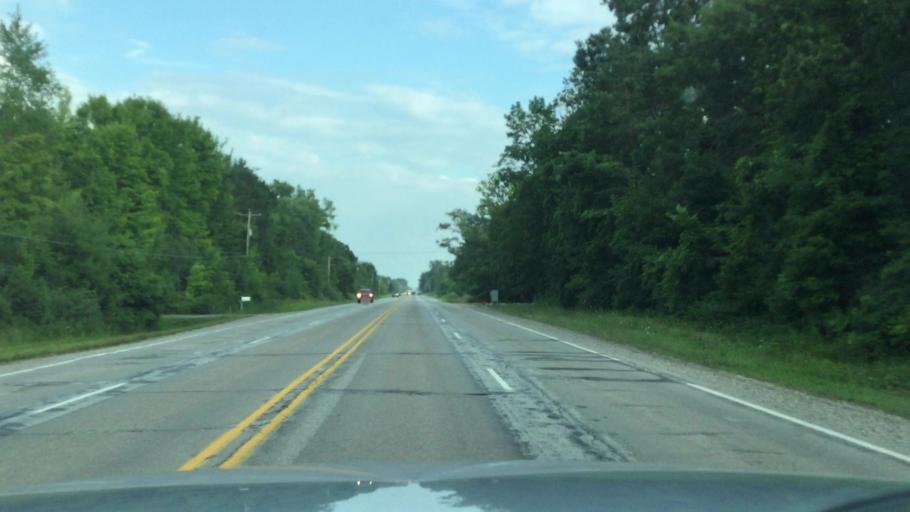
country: US
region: Michigan
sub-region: Saginaw County
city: Birch Run
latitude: 43.2773
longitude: -83.7898
